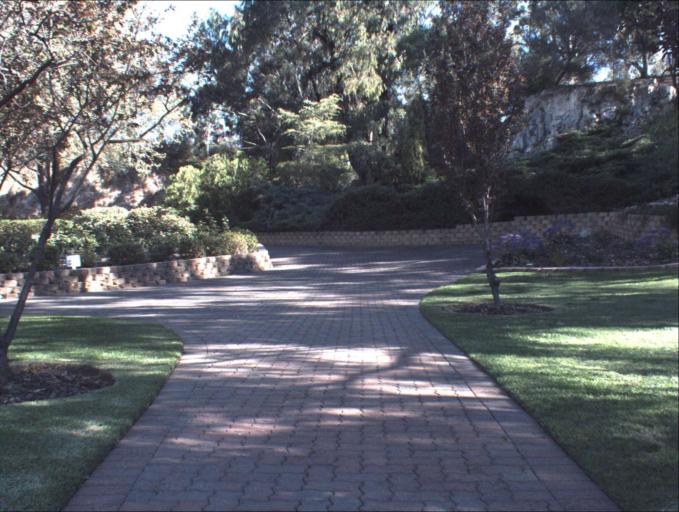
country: AU
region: South Australia
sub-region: Salisbury
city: Ingle Farm
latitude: -34.8409
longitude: 138.6258
